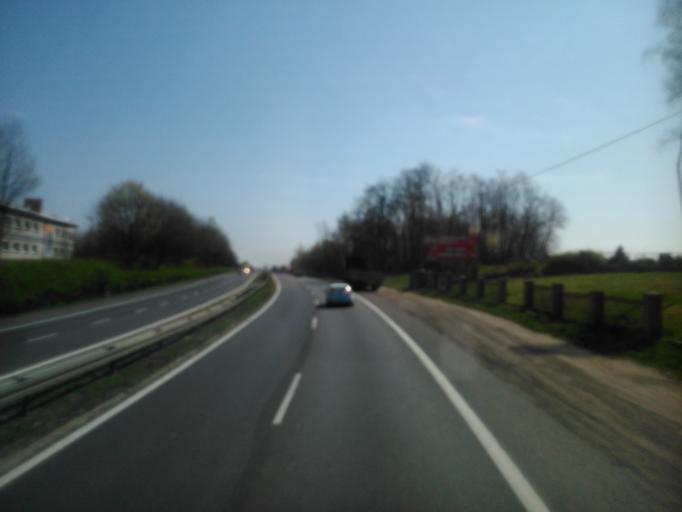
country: PL
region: Silesian Voivodeship
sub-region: Powiat czestochowski
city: Huta Stara B
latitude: 50.7440
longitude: 19.1537
